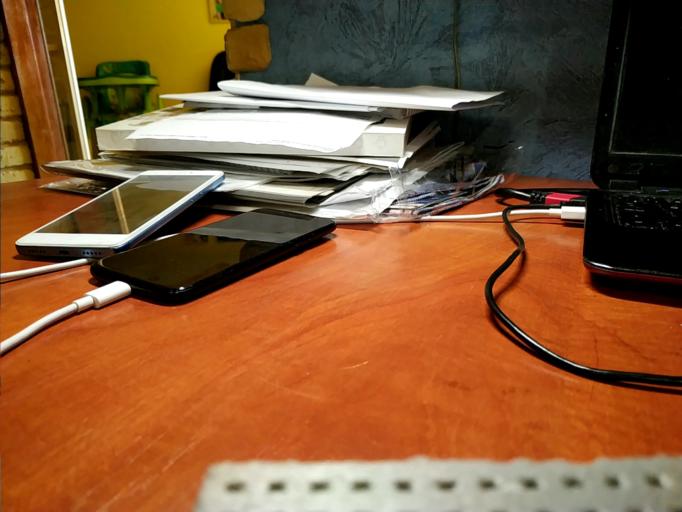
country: RU
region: Tverskaya
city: Kalashnikovo
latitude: 57.4048
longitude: 35.2041
